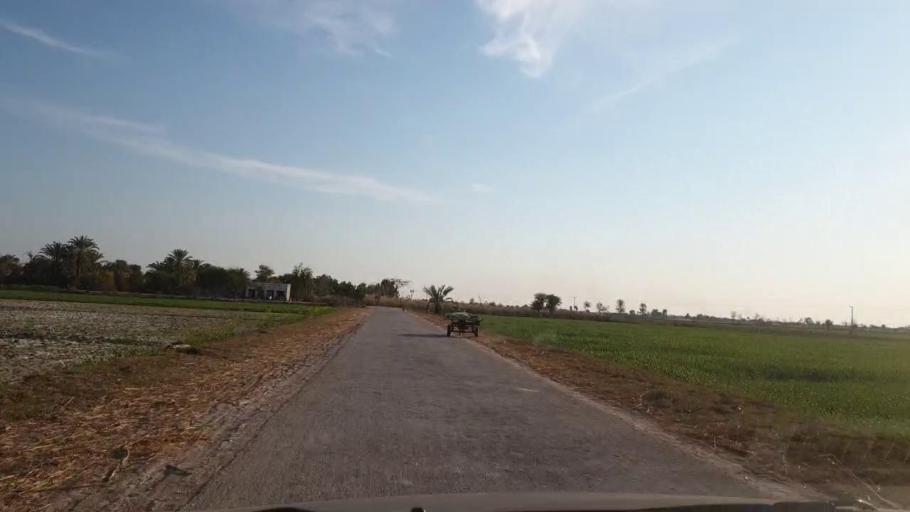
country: PK
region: Sindh
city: Khadro
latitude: 26.1910
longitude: 68.7469
